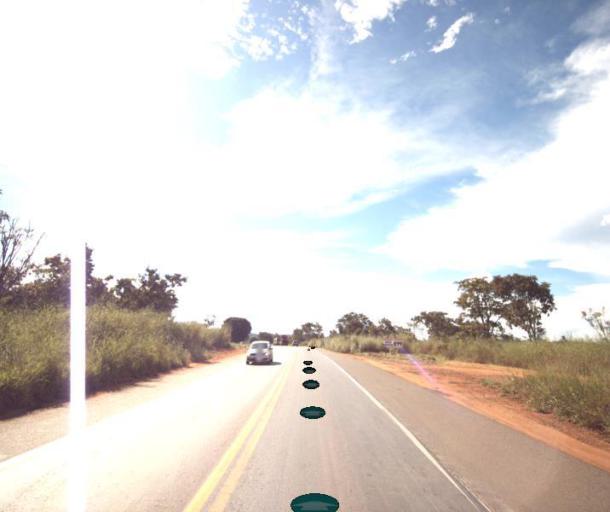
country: BR
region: Goias
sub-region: Jaragua
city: Jaragua
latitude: -15.5629
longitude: -49.4212
